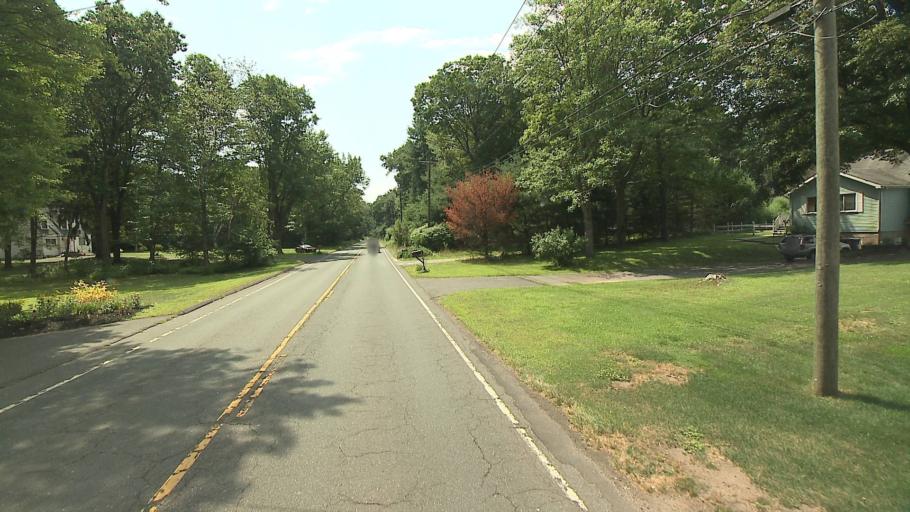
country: US
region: Connecticut
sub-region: Hartford County
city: Farmington
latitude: 41.7350
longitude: -72.8908
